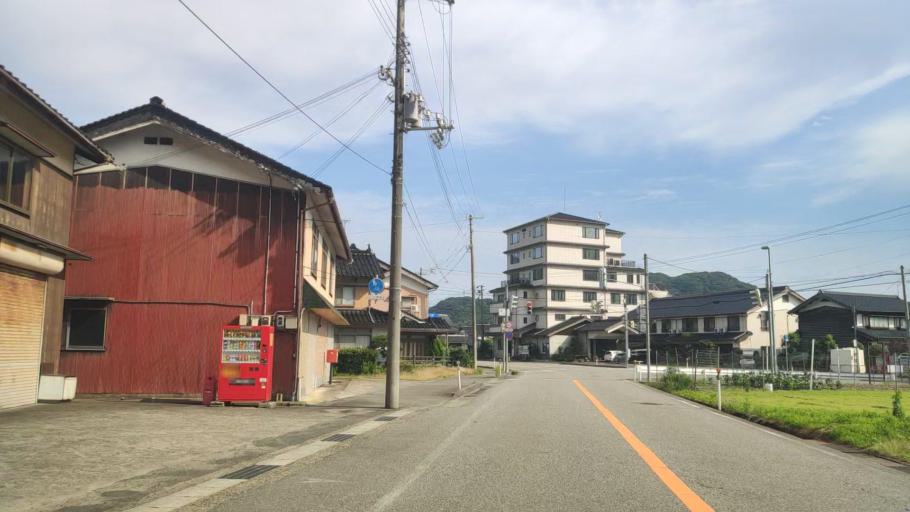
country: JP
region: Hyogo
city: Toyooka
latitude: 35.6401
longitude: 134.8358
